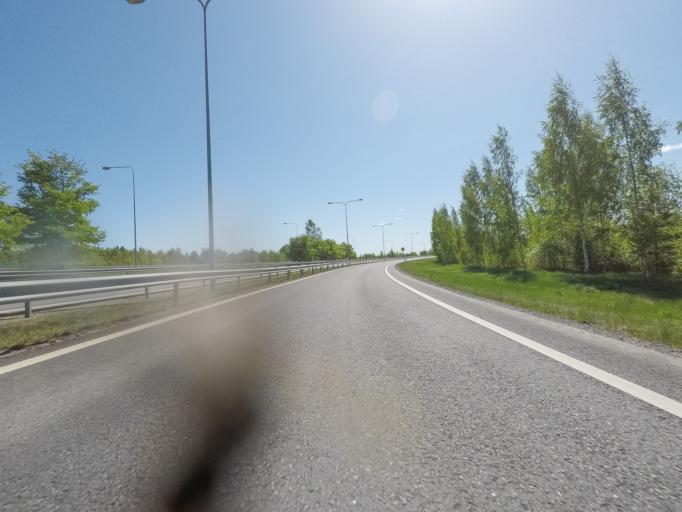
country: FI
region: Pirkanmaa
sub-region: Etelae-Pirkanmaa
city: Toijala
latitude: 61.2065
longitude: 23.8427
